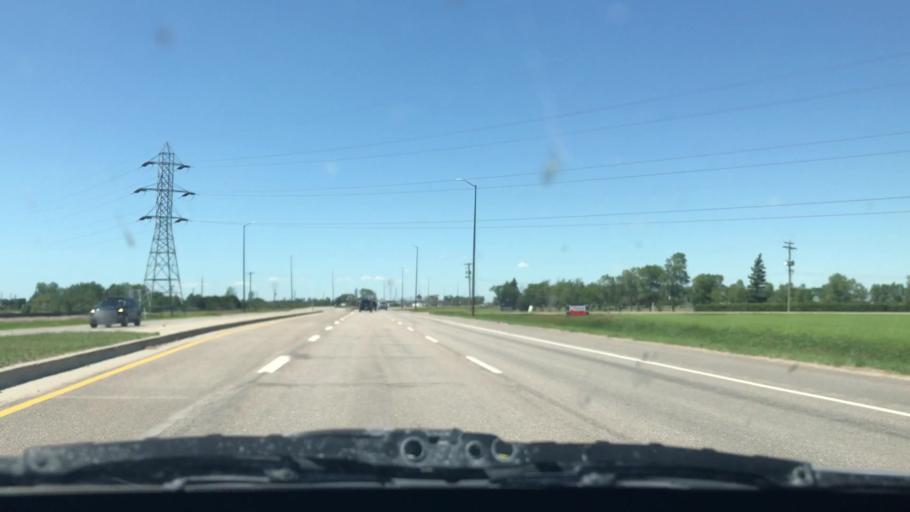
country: CA
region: Manitoba
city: Winnipeg
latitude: 49.8404
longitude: -96.9849
